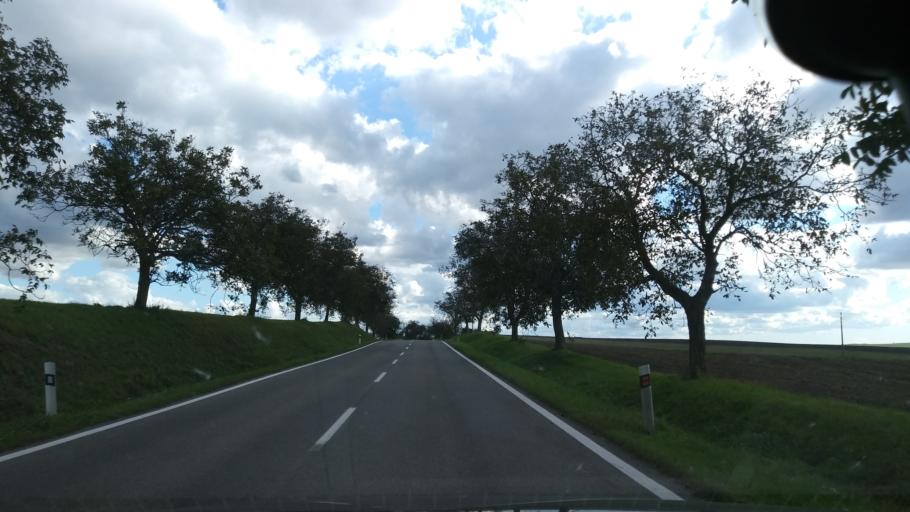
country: SK
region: Trnavsky
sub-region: Okres Skalica
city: Holic
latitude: 48.7951
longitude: 17.1675
